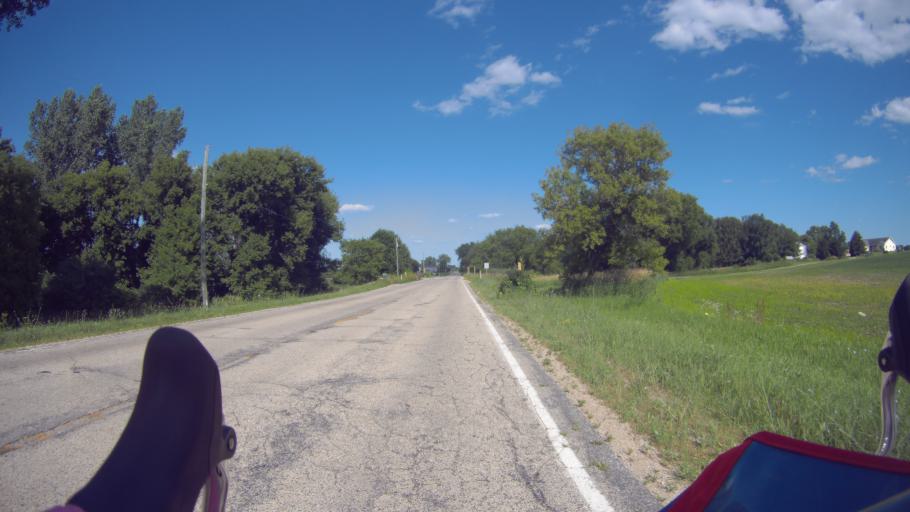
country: US
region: Wisconsin
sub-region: Green County
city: Brooklyn
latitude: 42.8933
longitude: -89.2990
